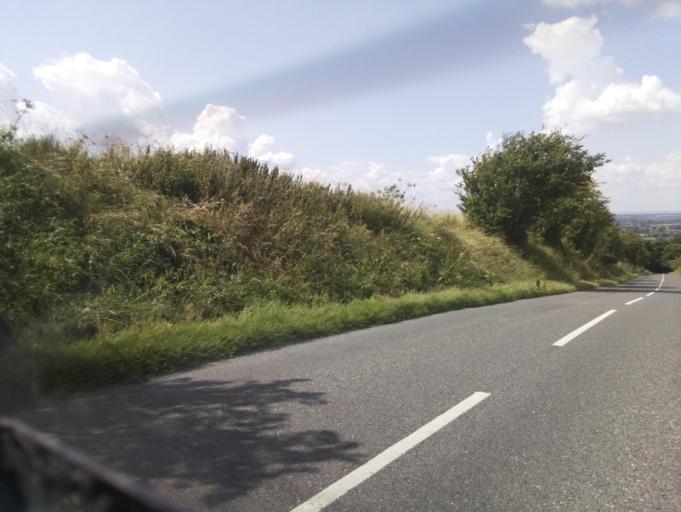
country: GB
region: England
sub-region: Borough of Swindon
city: Bishopstone
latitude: 51.5602
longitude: -1.6117
